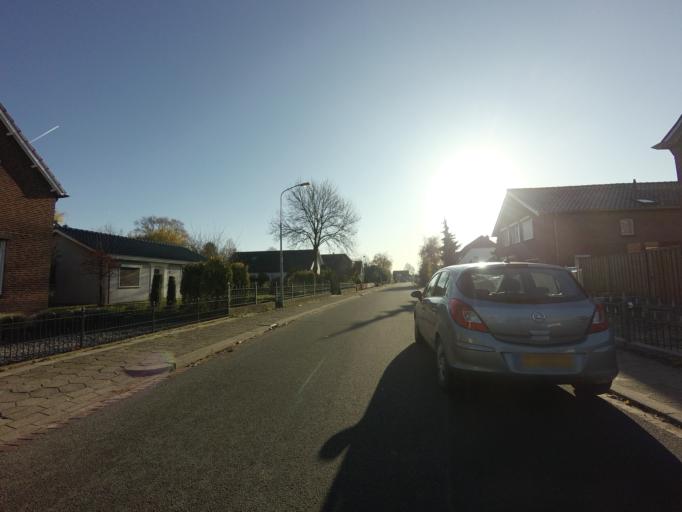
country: NL
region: Gelderland
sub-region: Gemeente Maasdriel
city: Heerewaarden
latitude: 51.7662
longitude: 5.3426
